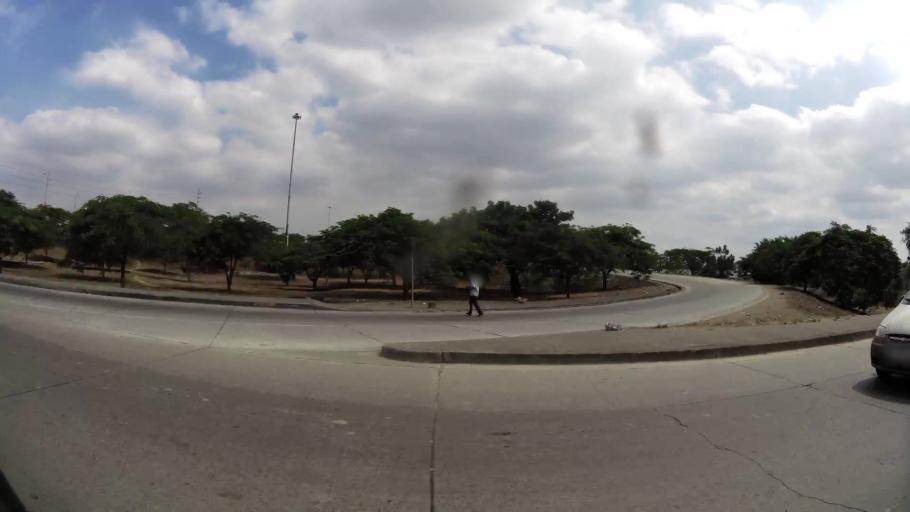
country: EC
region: Guayas
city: Eloy Alfaro
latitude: -2.0739
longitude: -79.9204
